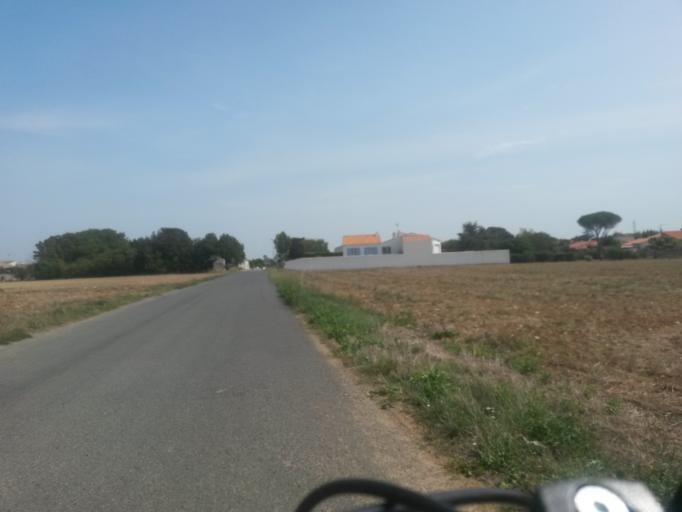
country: FR
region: Poitou-Charentes
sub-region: Departement de la Charente-Maritime
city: Saint-Xandre
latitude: 46.2017
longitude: -1.1138
